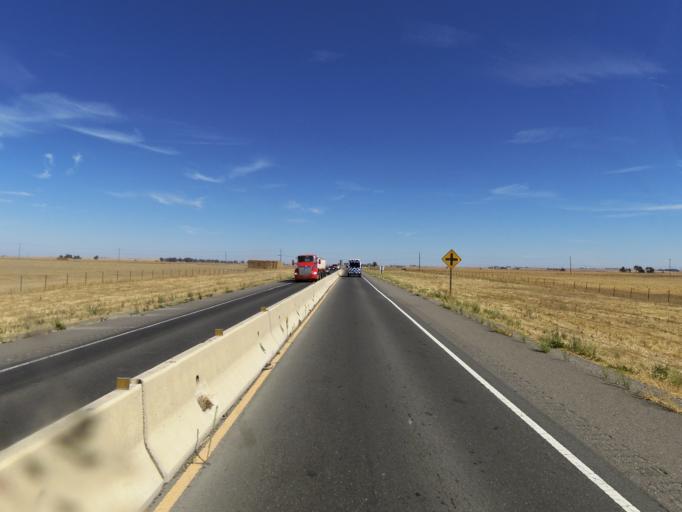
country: US
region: California
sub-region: Solano County
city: Suisun
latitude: 38.2285
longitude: -121.9557
